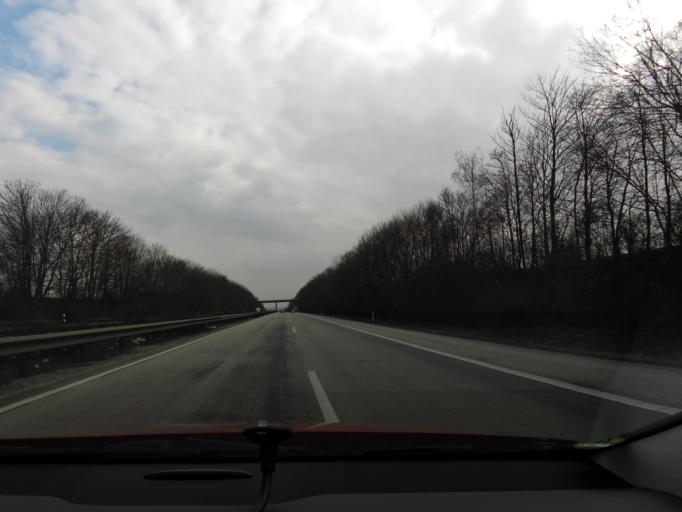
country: DE
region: Rheinland-Pfalz
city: Zotzenheim
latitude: 49.8563
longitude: 7.9736
